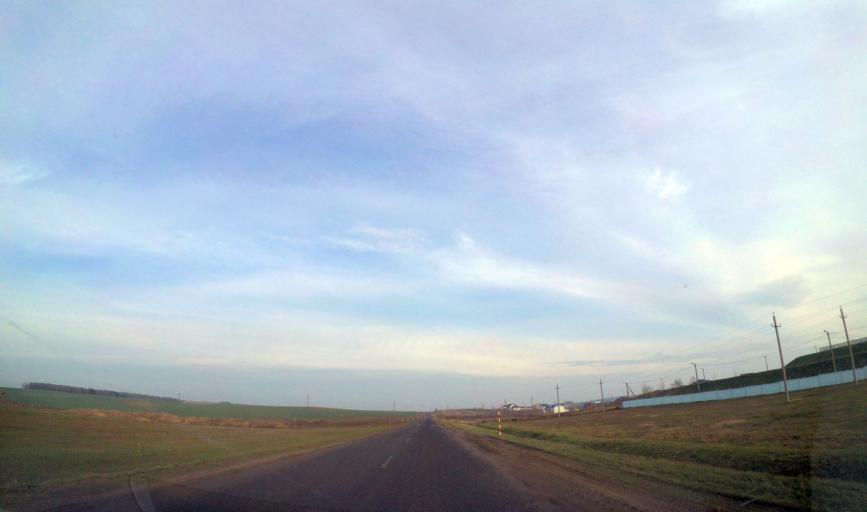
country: BY
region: Grodnenskaya
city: Hrodna
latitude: 53.7201
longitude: 23.8868
